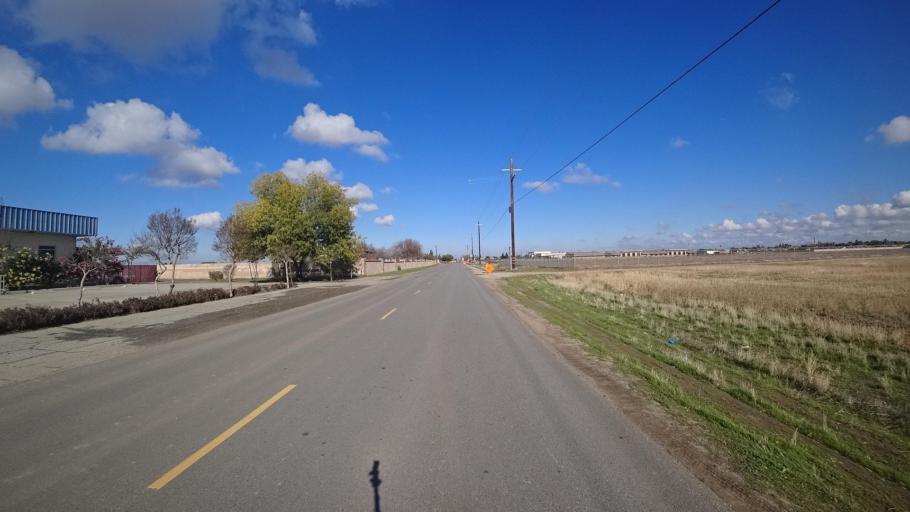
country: US
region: California
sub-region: Kern County
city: McFarland
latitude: 35.6638
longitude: -119.2396
